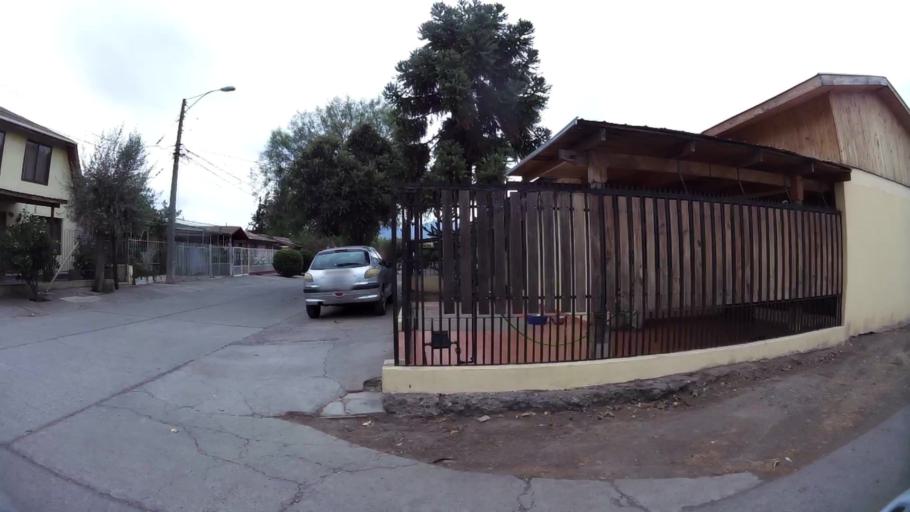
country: CL
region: O'Higgins
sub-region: Provincia de Cachapoal
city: Rancagua
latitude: -34.1518
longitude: -70.7378
